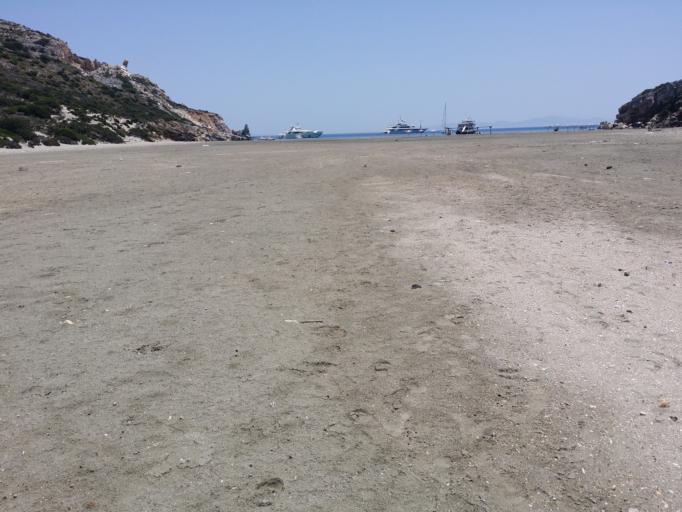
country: GR
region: South Aegean
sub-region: Nomos Kykladon
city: Antiparos
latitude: 36.9571
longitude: 24.9988
